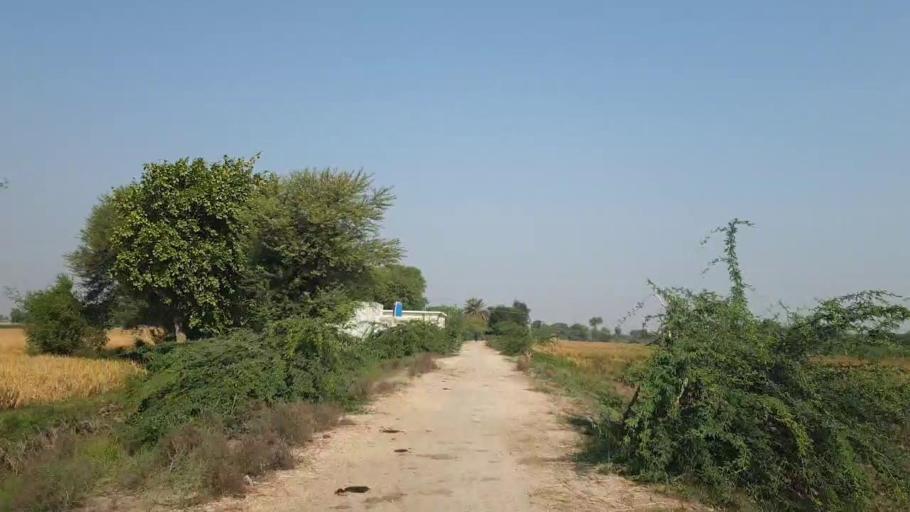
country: PK
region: Sindh
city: Matli
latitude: 25.0002
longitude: 68.6221
